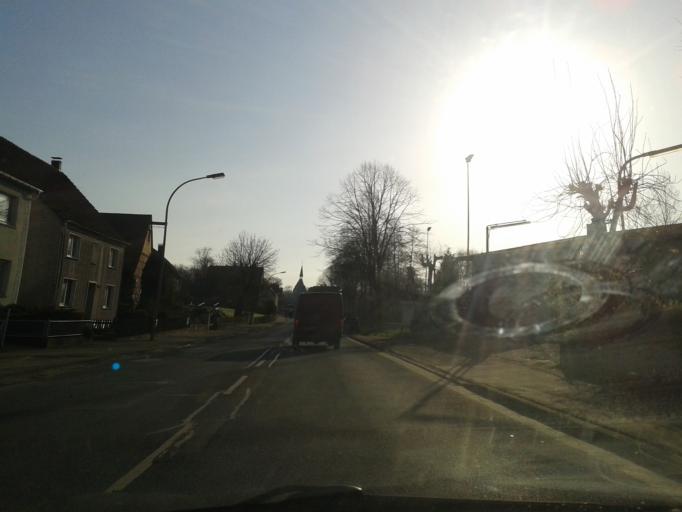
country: DE
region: North Rhine-Westphalia
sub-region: Regierungsbezirk Detmold
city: Steinheim
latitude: 51.8967
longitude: 9.0947
